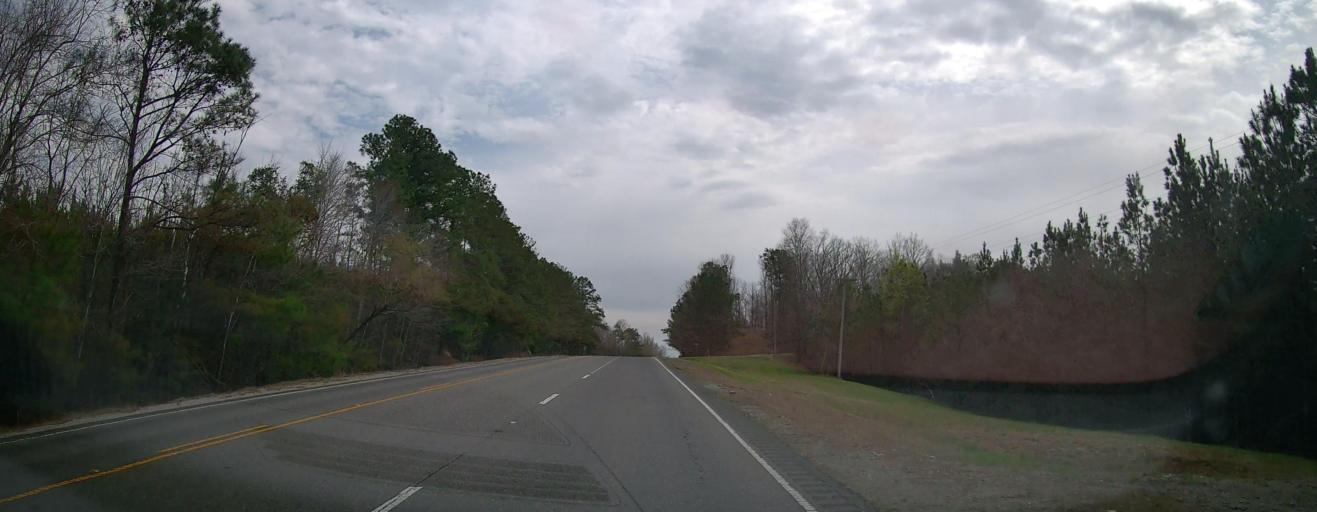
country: US
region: Alabama
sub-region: Marion County
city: Hamilton
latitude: 34.0564
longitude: -87.9667
